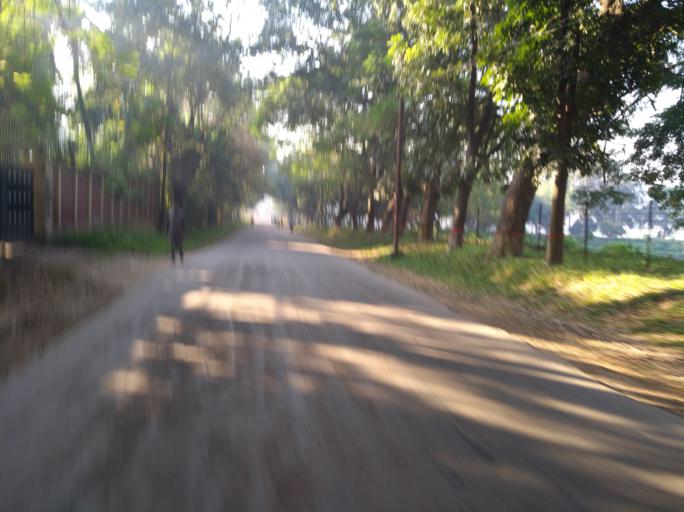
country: BD
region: Dhaka
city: Tungi
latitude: 23.8886
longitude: 90.2678
